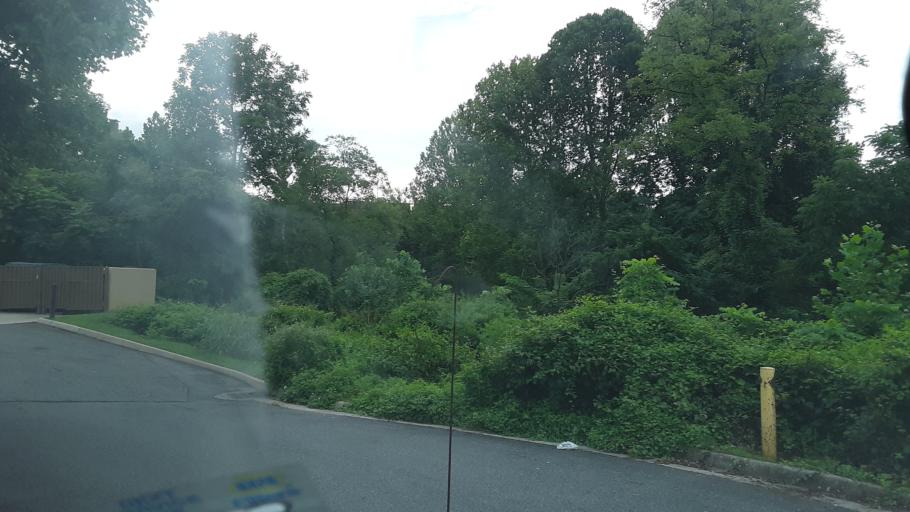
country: US
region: Virginia
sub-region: City of Charlottesville
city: Charlottesville
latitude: 38.0111
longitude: -78.5027
